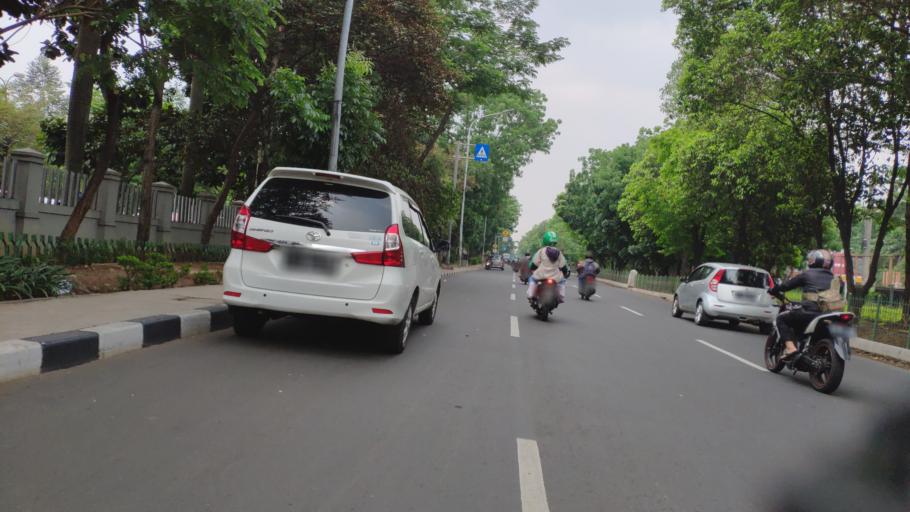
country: ID
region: West Java
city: Depok
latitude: -6.3413
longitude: 106.8335
